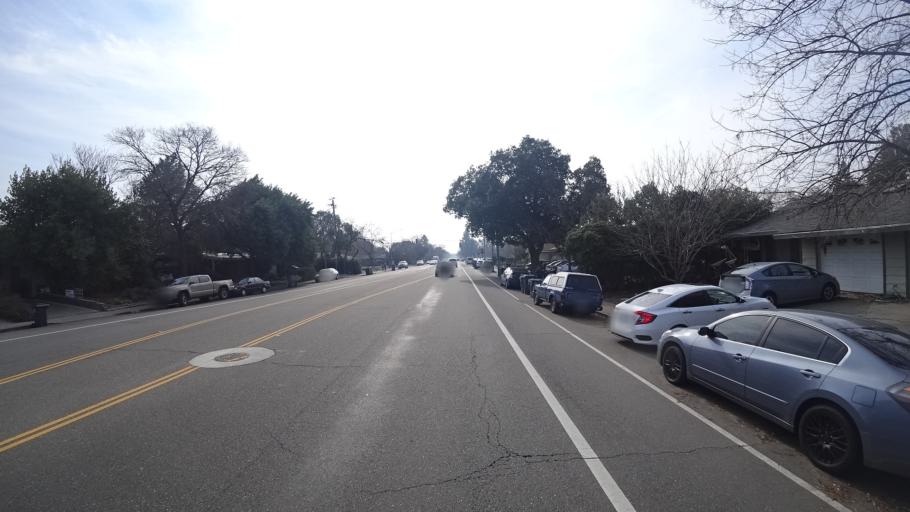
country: US
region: California
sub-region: Yolo County
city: Davis
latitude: 38.5557
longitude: -121.7586
